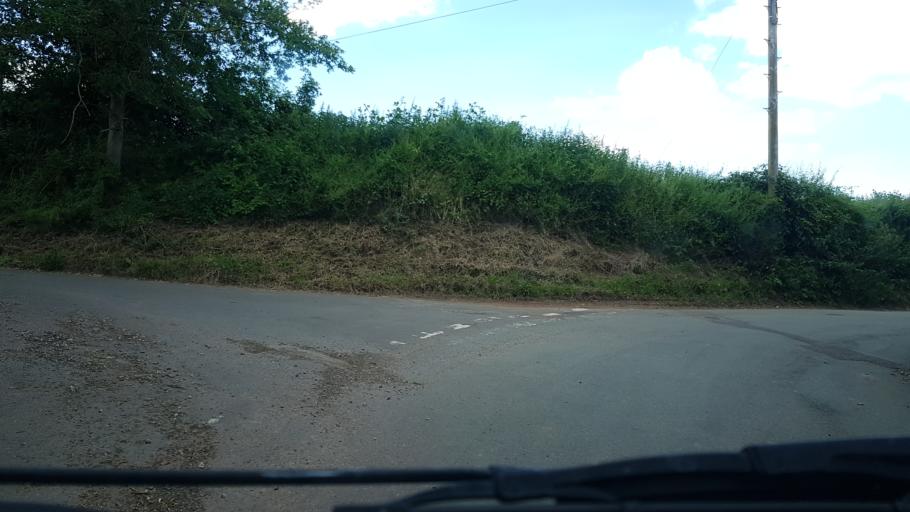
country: GB
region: England
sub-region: Shropshire
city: Romsley
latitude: 52.4616
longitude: -2.2627
